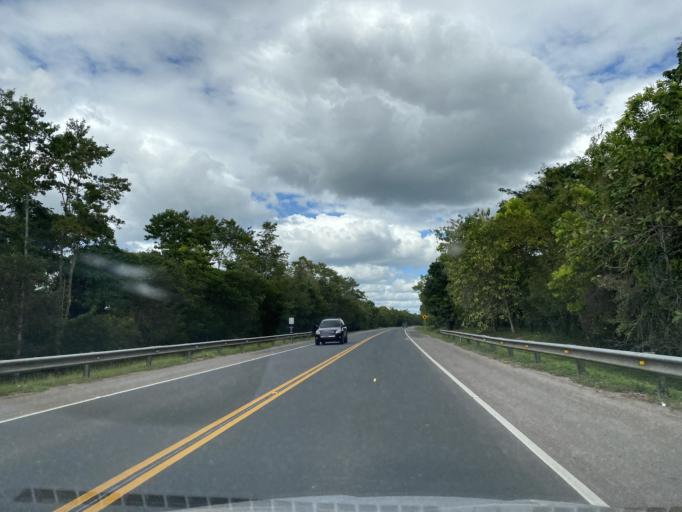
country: DO
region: Santo Domingo
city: Guerra
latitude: 18.6024
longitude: -69.7708
